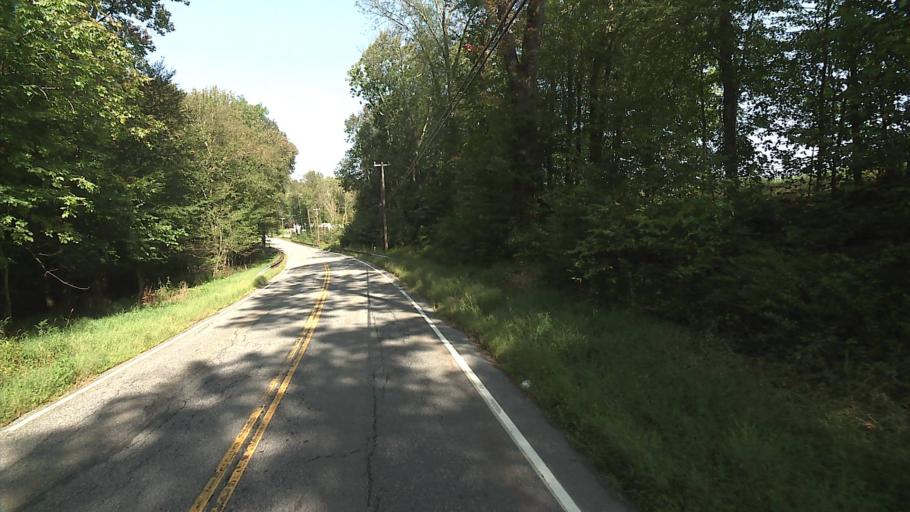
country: US
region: Connecticut
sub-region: Windham County
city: Quinebaug
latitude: 42.0112
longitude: -72.0022
